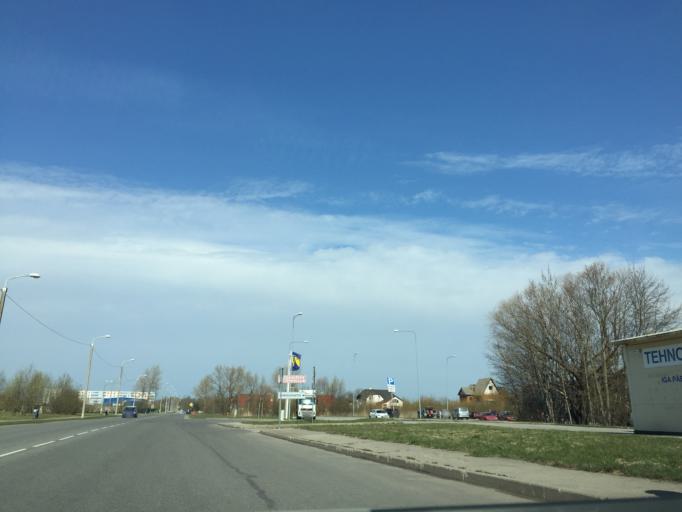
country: EE
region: Ida-Virumaa
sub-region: Narva linn
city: Narva
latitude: 59.3883
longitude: 28.1876
